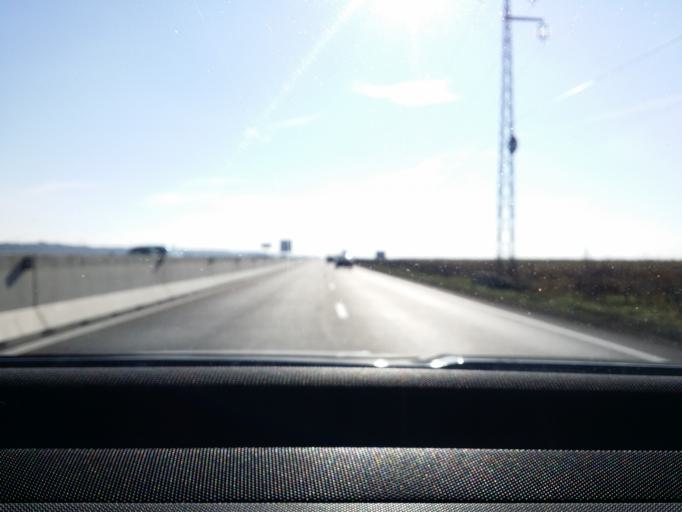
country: RO
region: Prahova
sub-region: Comuna Banesti
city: Banesti
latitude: 45.0903
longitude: 25.7689
